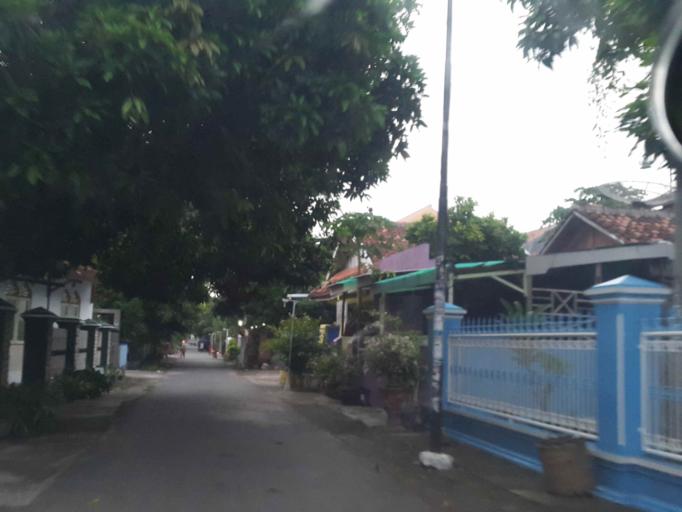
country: ID
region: Central Java
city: Kabongan Lor
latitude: -6.7063
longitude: 111.3557
